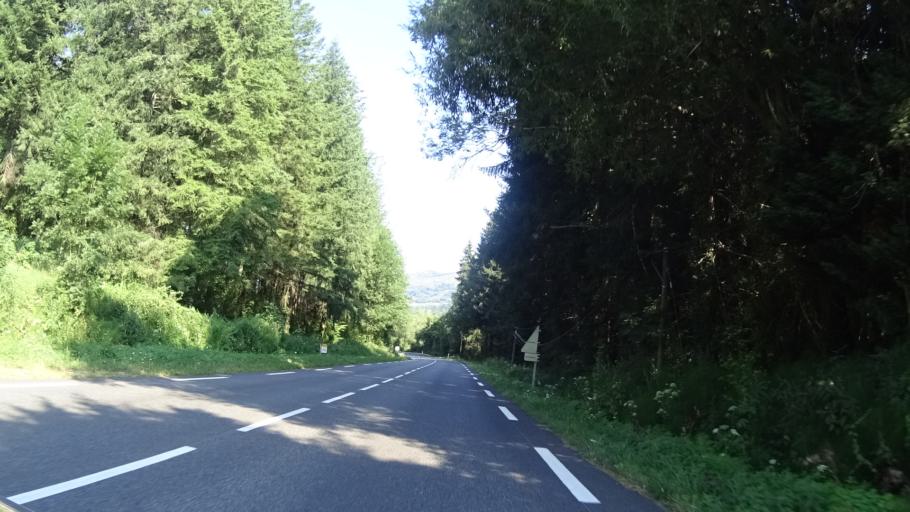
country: FR
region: Midi-Pyrenees
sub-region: Departement de l'Ariege
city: Lavelanet
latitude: 42.9183
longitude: 1.7572
